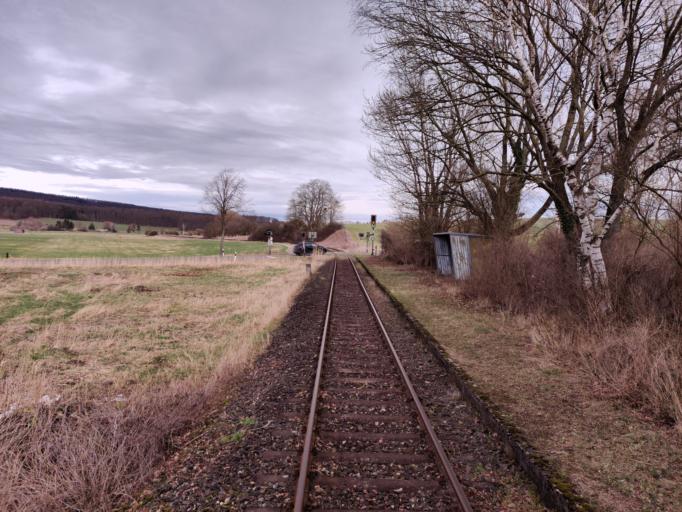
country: DE
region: Lower Saxony
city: Bockenem
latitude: 52.0381
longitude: 10.1221
